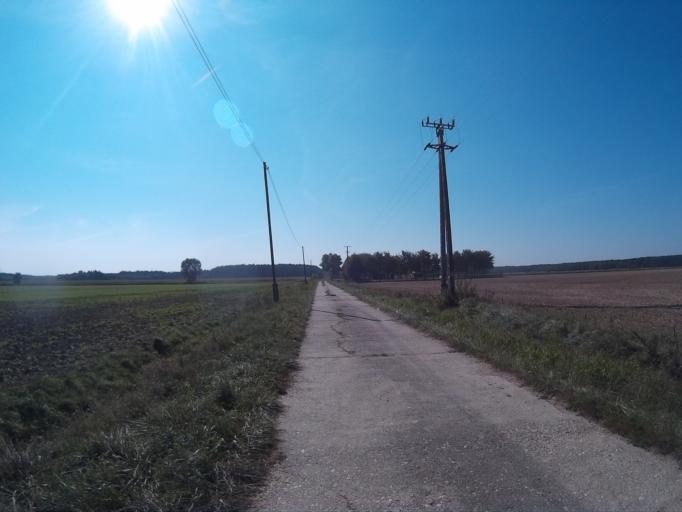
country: HU
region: Vas
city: Kormend
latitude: 47.0757
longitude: 16.6292
